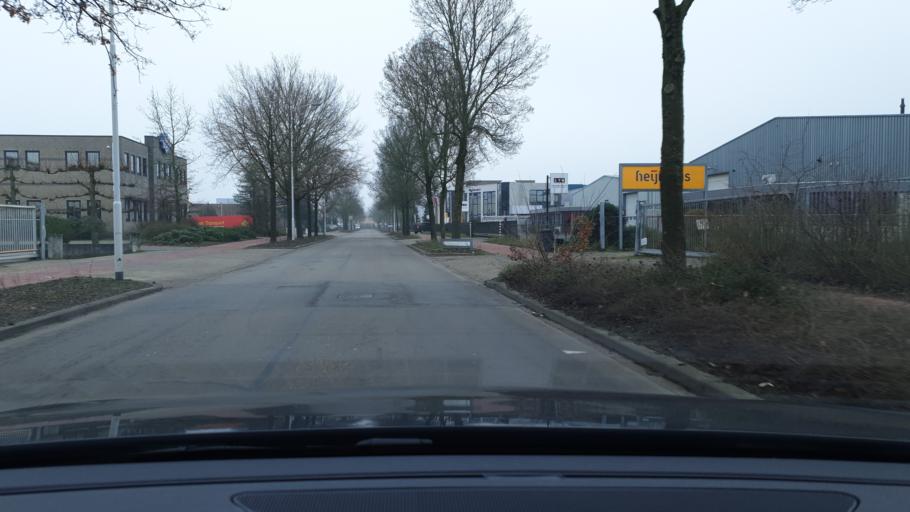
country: NL
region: North Brabant
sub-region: Gemeente Best
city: Best
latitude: 51.4928
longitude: 5.4021
